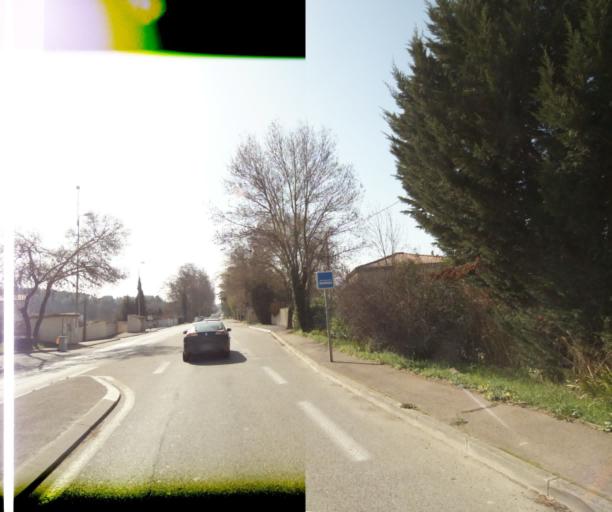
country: FR
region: Provence-Alpes-Cote d'Azur
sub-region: Departement des Bouches-du-Rhone
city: Bouc-Bel-Air
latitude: 43.4576
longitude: 5.4038
